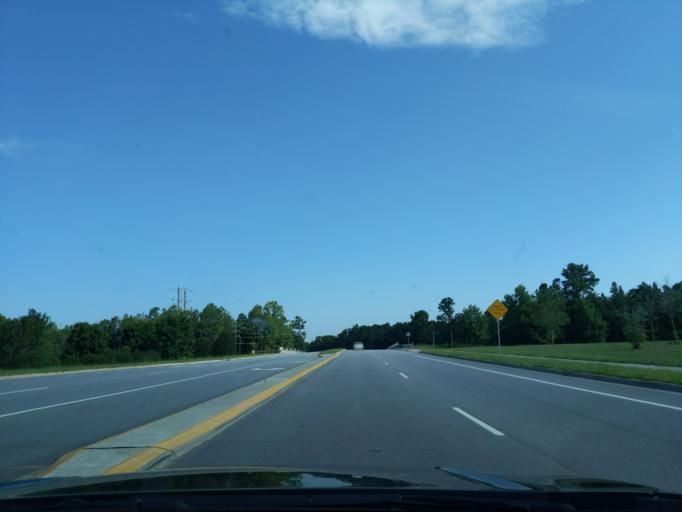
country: US
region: South Carolina
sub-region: Greenville County
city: Mauldin
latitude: 34.8191
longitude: -82.3171
